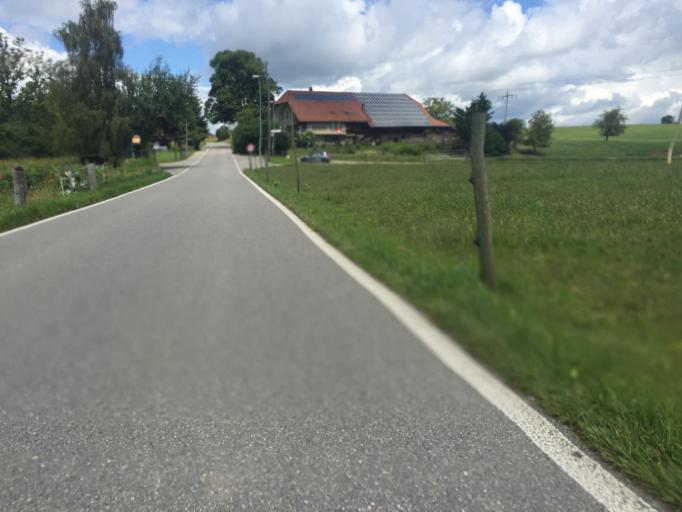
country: CH
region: Bern
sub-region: Bern-Mittelland District
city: Kirchlindach
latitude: 46.9926
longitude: 7.4120
